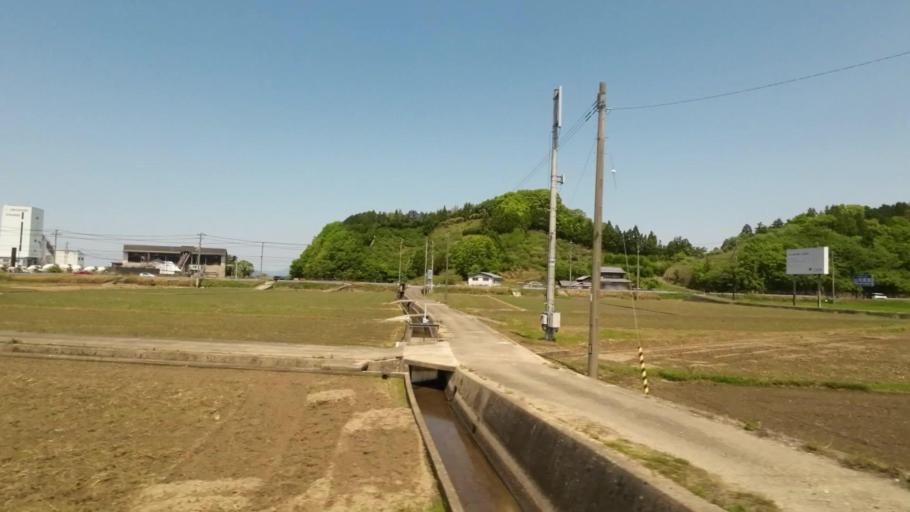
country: JP
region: Ehime
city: Hojo
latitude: 34.0607
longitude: 132.8956
